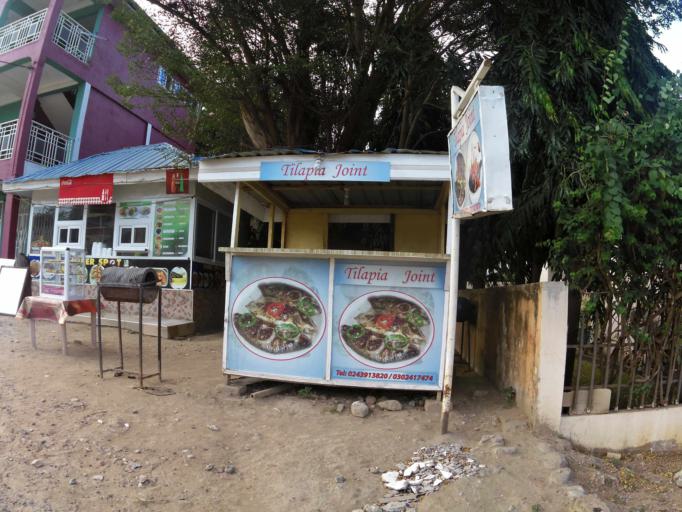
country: GH
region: Greater Accra
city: Dome
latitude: 5.6453
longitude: -0.2137
